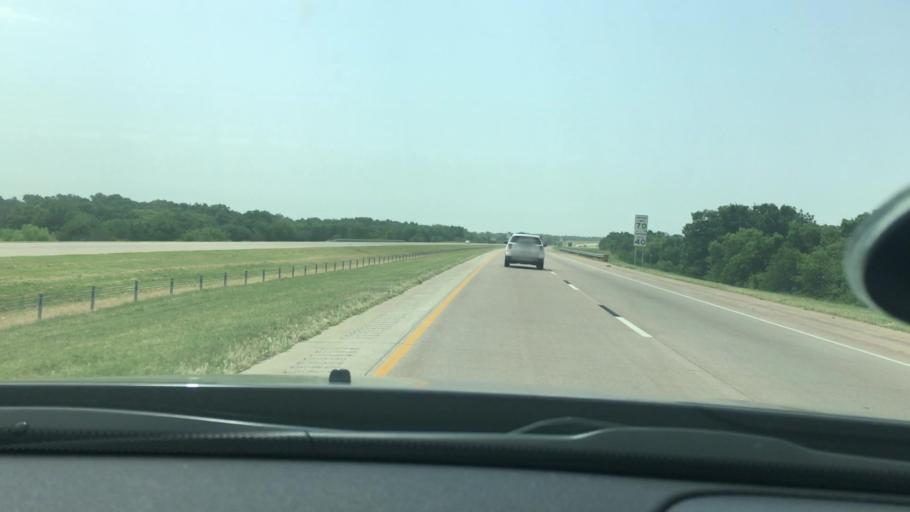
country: US
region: Oklahoma
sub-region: Garvin County
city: Pauls Valley
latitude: 34.6981
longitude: -97.2382
